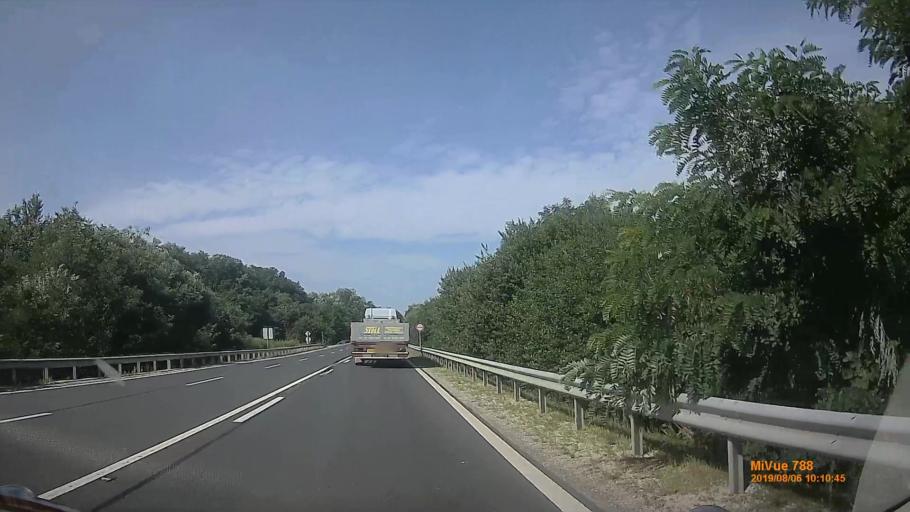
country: HU
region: Vas
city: Vasvar
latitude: 47.0973
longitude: 16.9016
